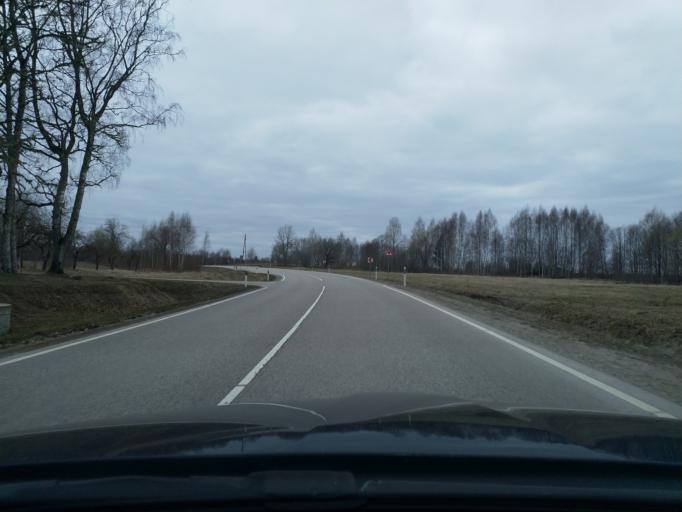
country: LV
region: Talsu Rajons
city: Sabile
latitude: 56.9494
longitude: 22.4750
